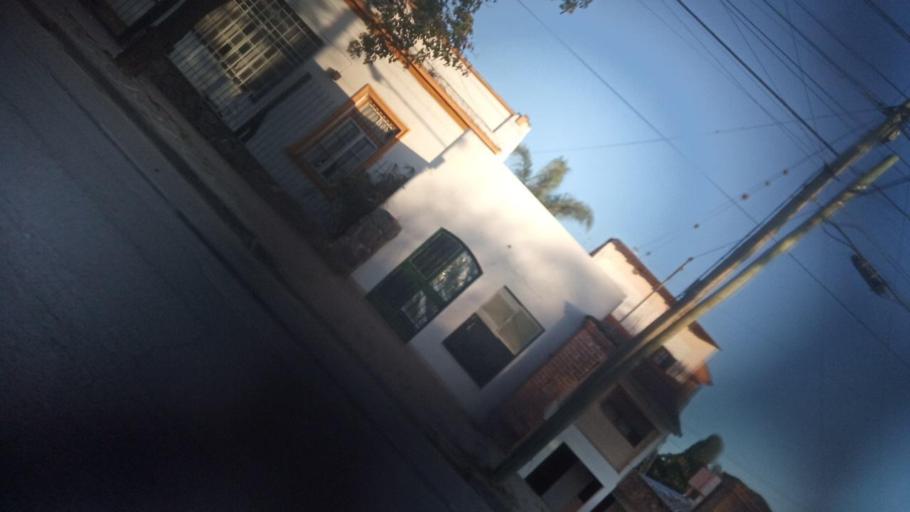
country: AR
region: Jujuy
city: San Salvador de Jujuy
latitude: -24.1692
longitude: -65.3152
